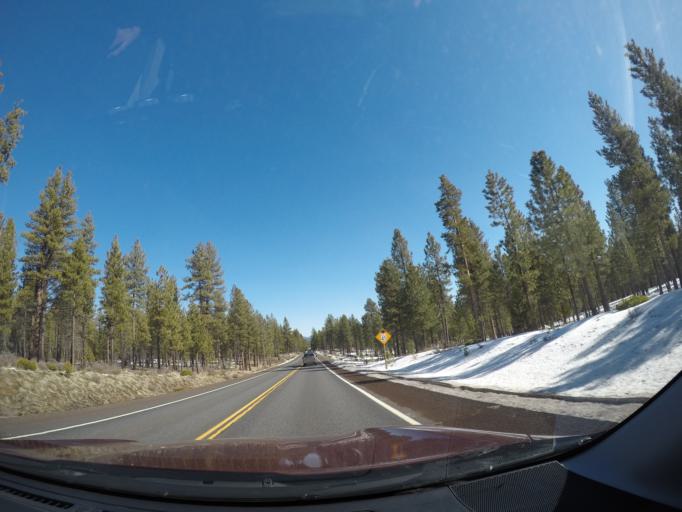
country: US
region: Oregon
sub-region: Deschutes County
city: Three Rivers
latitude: 43.8627
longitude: -121.4856
